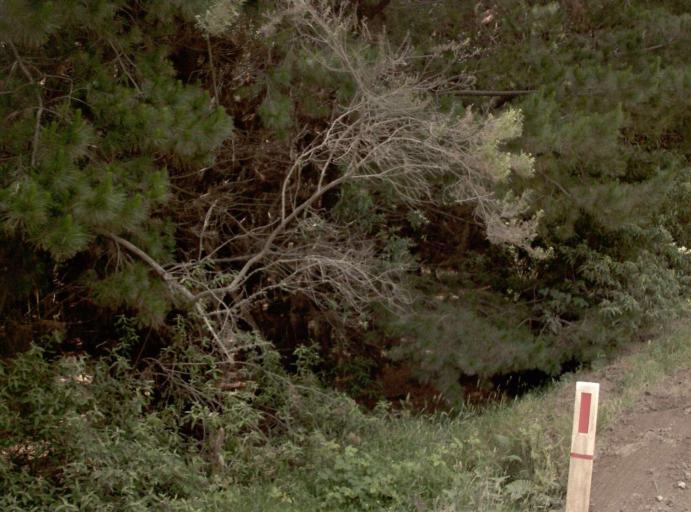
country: AU
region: Victoria
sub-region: Latrobe
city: Traralgon
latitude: -38.4120
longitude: 146.6206
